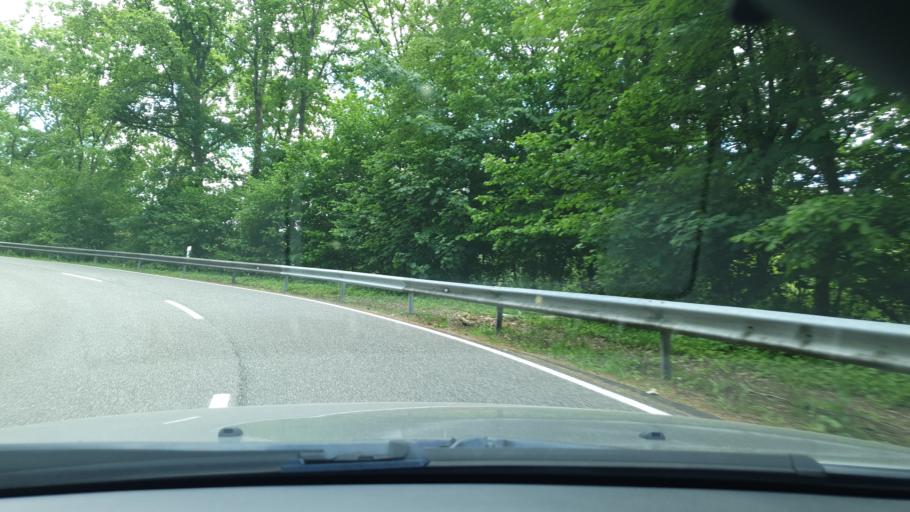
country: DE
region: Rheinland-Pfalz
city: Battweiler
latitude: 49.2778
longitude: 7.4546
